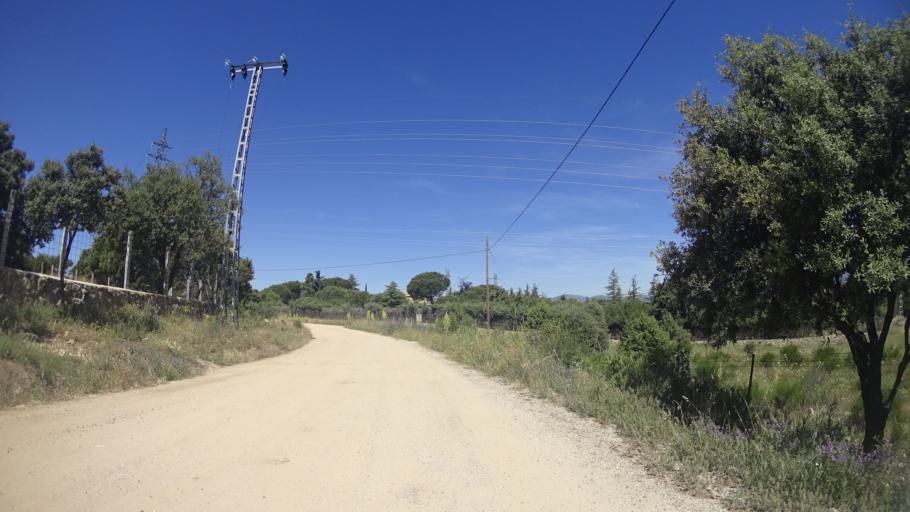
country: ES
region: Madrid
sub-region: Provincia de Madrid
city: Galapagar
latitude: 40.5980
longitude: -3.9997
